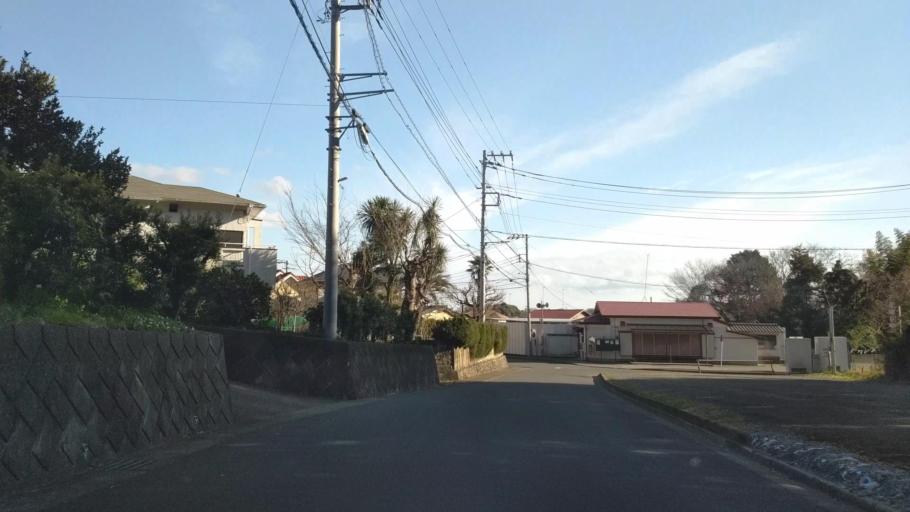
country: JP
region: Kanagawa
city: Hadano
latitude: 35.3707
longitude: 139.2513
